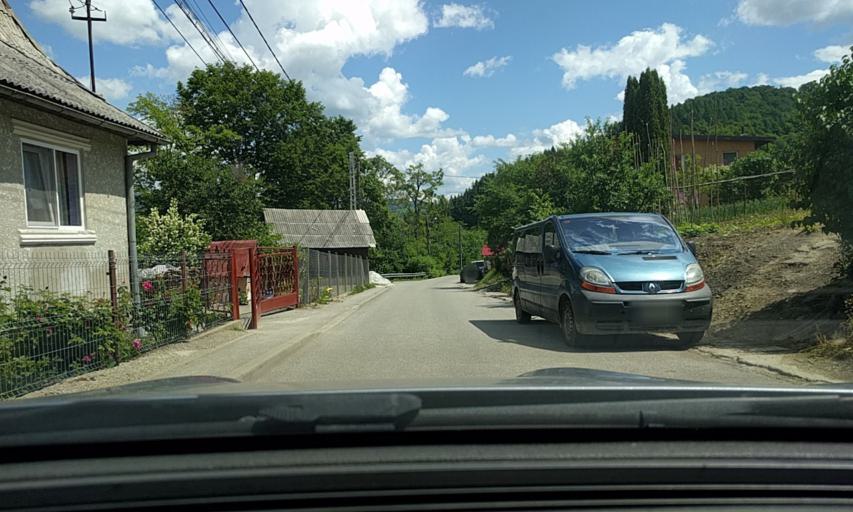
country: RO
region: Bistrita-Nasaud
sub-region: Oras Nasaud
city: Nasaud
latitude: 47.2774
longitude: 24.4197
